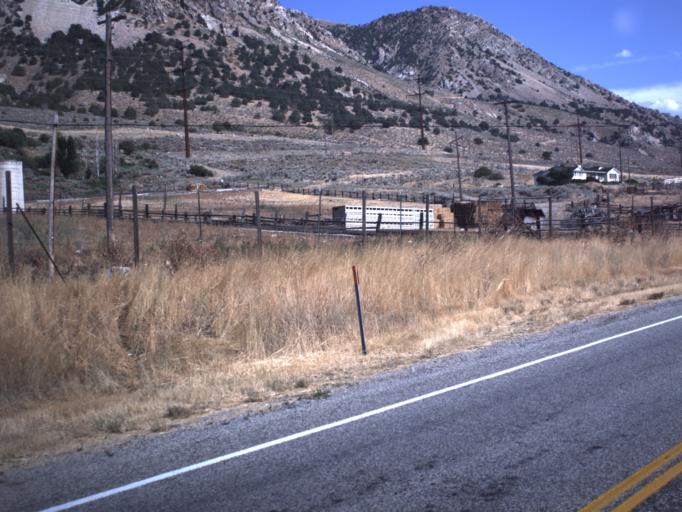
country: US
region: Utah
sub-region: Box Elder County
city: Brigham City
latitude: 41.5459
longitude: -112.0156
